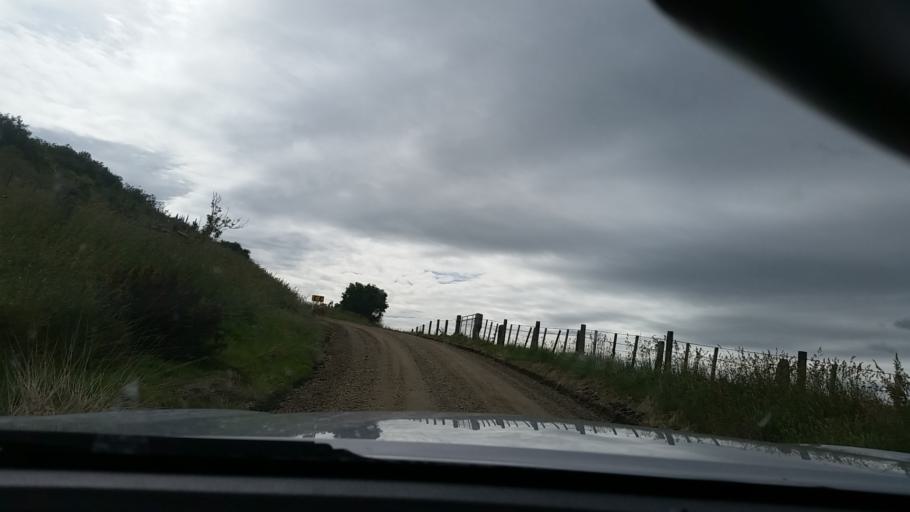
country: NZ
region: Southland
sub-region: Gore District
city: Gore
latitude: -46.2610
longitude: 168.8946
